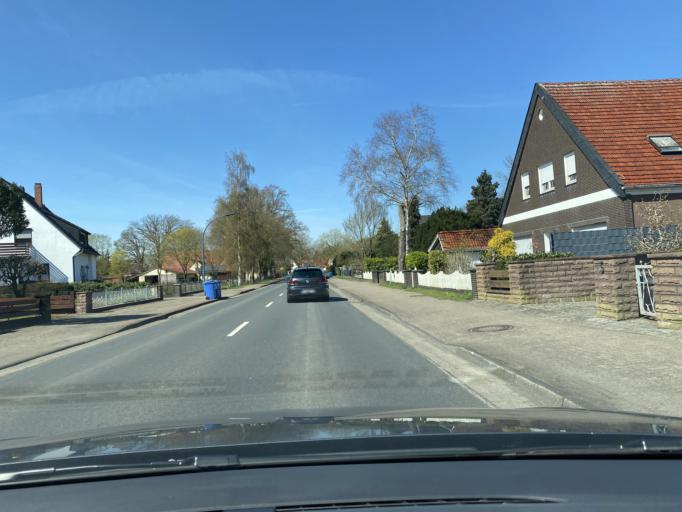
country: DE
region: Lower Saxony
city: Oyten
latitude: 53.0720
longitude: 9.0206
